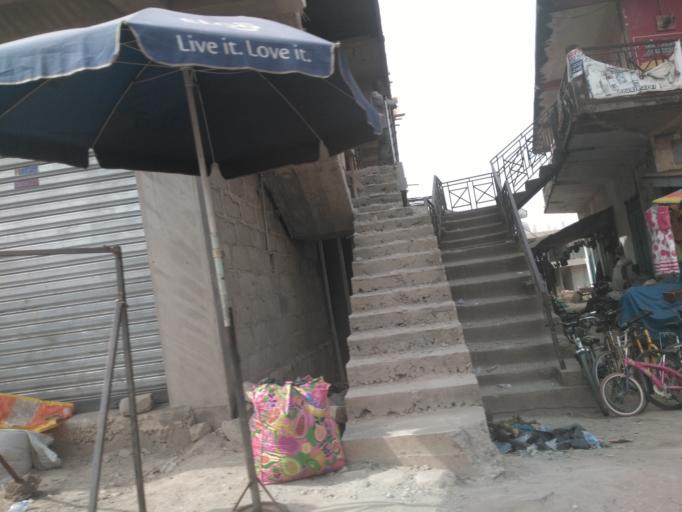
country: GH
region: Ashanti
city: Kumasi
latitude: 6.6960
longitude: -1.6163
